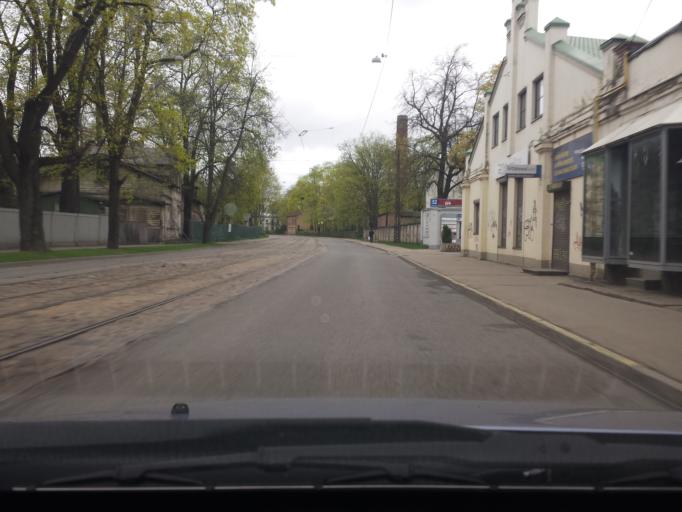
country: LV
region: Riga
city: Riga
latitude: 56.9540
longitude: 24.0630
